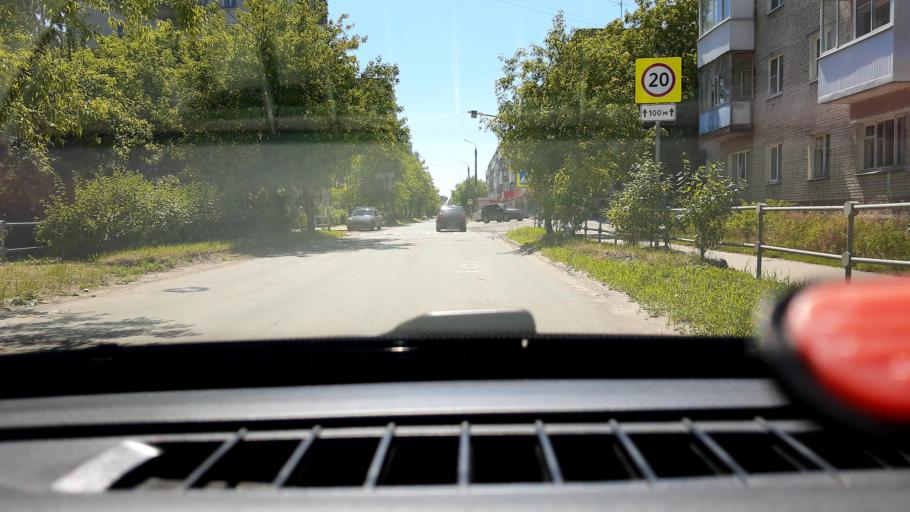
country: RU
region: Nizjnij Novgorod
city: Dzerzhinsk
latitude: 56.2527
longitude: 43.4742
